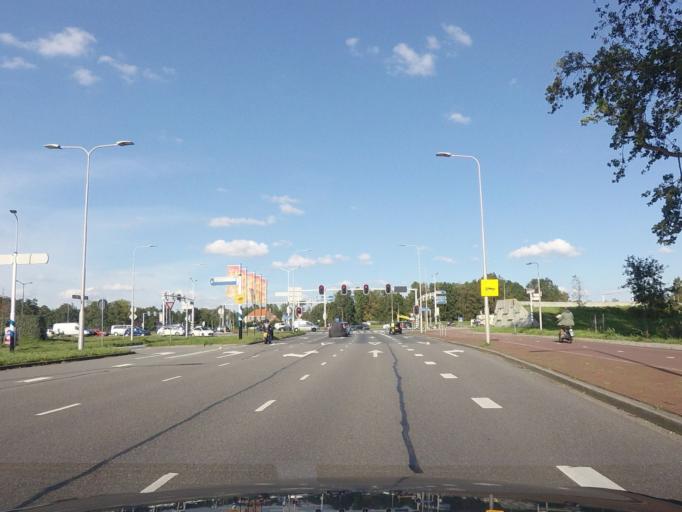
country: NL
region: South Holland
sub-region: Gemeente Leidschendam-Voorburg
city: Voorburg
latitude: 52.1010
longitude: 4.3637
